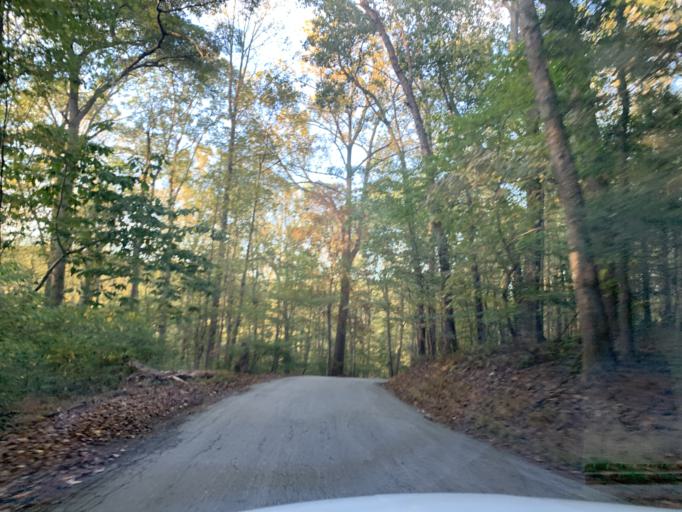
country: US
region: Maryland
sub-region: Harford County
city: Fallston
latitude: 39.5034
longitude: -76.4335
